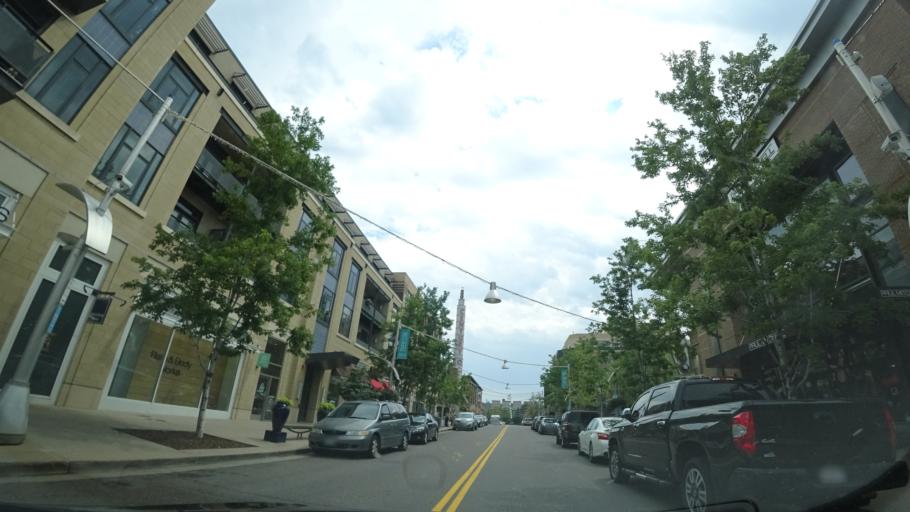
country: US
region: Colorado
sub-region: Jefferson County
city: Lakewood
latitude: 39.7092
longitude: -105.0769
